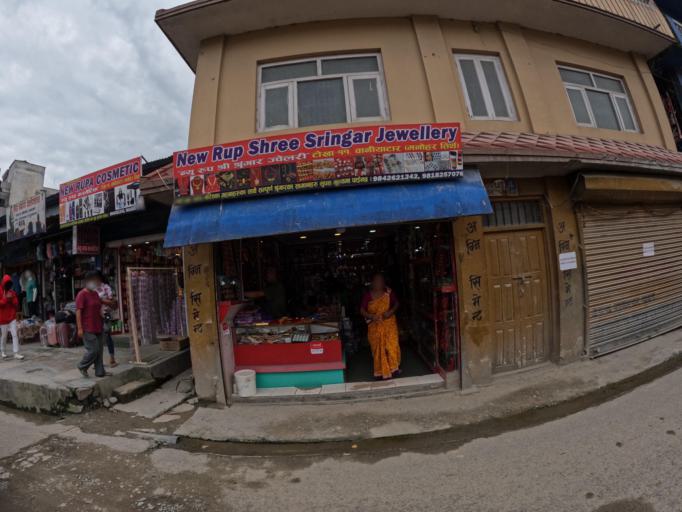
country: NP
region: Central Region
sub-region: Bagmati Zone
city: Kathmandu
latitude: 27.7442
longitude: 85.3159
